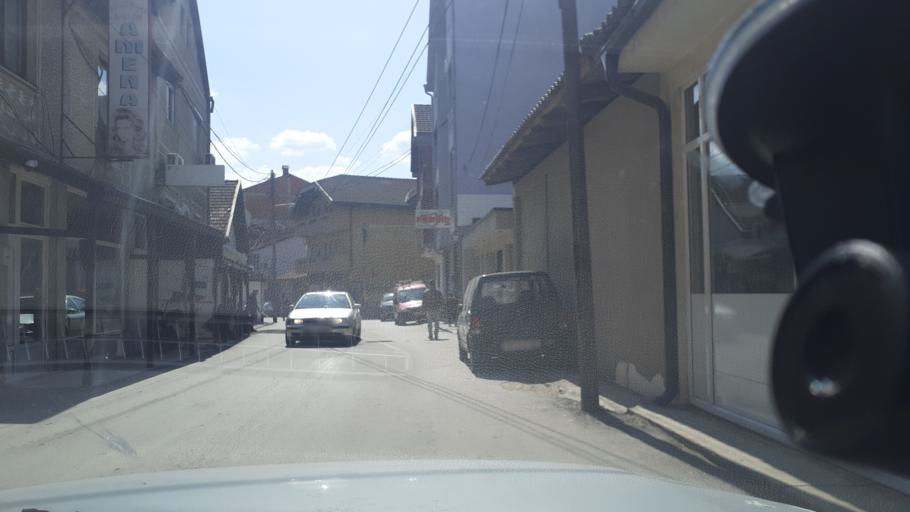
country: MK
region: Tetovo
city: Tetovo
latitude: 42.0049
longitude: 20.9669
